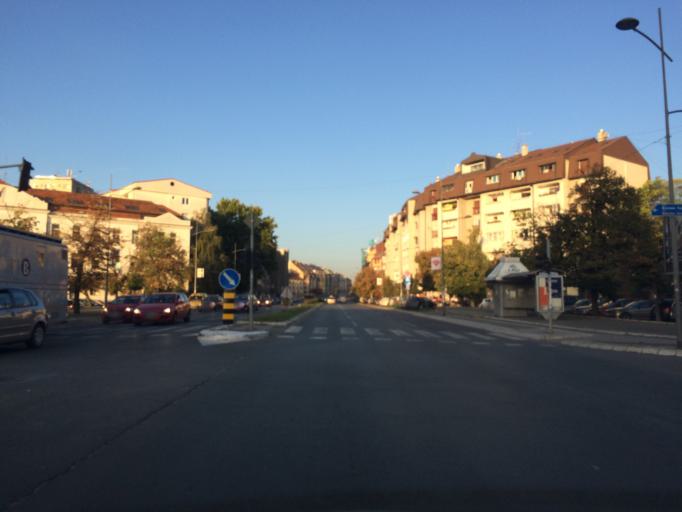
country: RS
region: Autonomna Pokrajina Vojvodina
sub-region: Juznobacki Okrug
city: Novi Sad
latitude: 45.2489
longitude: 19.8429
